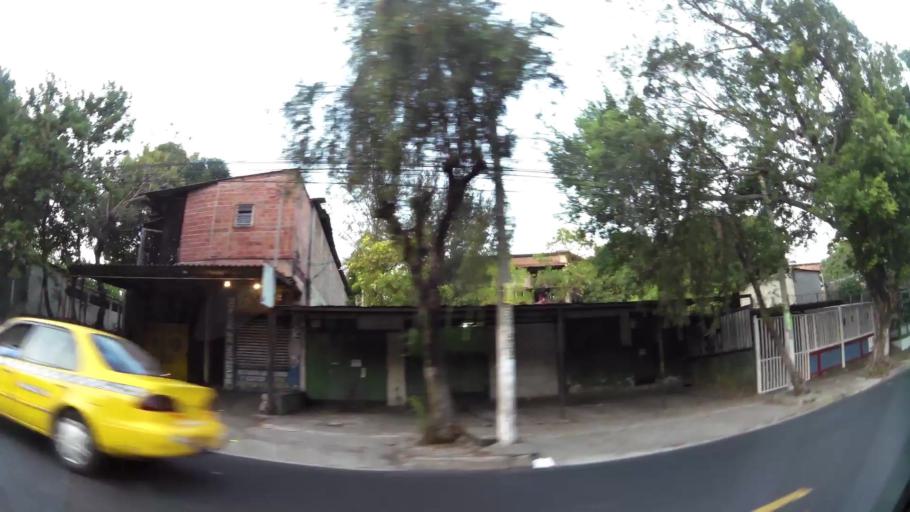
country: SV
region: San Salvador
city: Delgado
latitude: 13.7090
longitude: -89.1805
